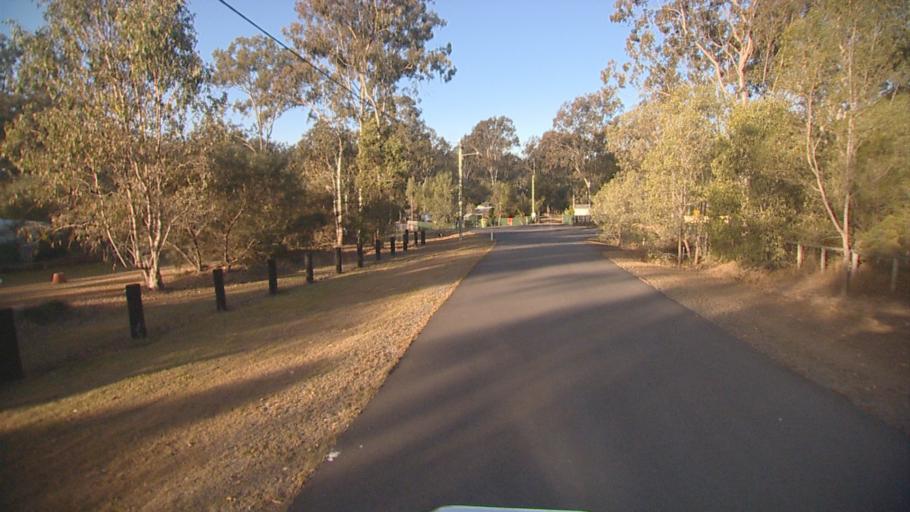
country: AU
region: Queensland
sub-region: Logan
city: Cedar Vale
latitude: -27.8536
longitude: 153.0975
